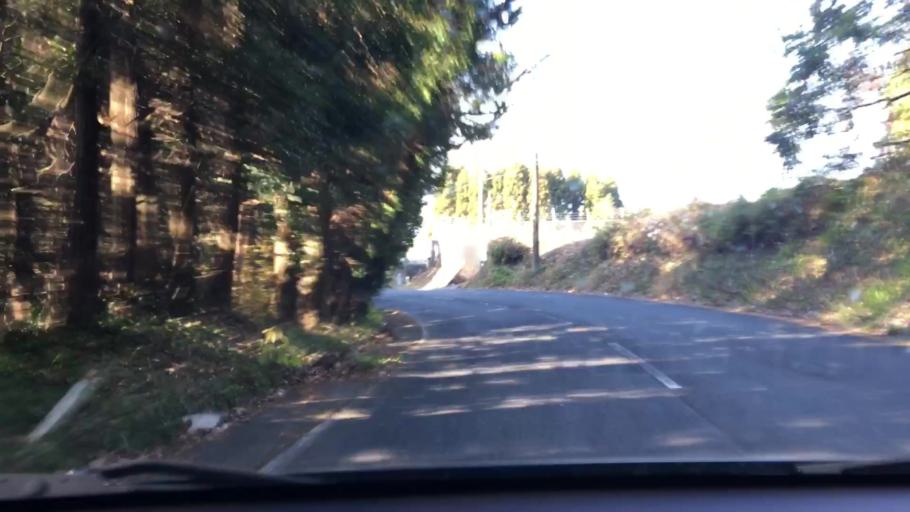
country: JP
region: Kagoshima
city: Kokubu-matsuki
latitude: 31.6663
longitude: 130.8245
